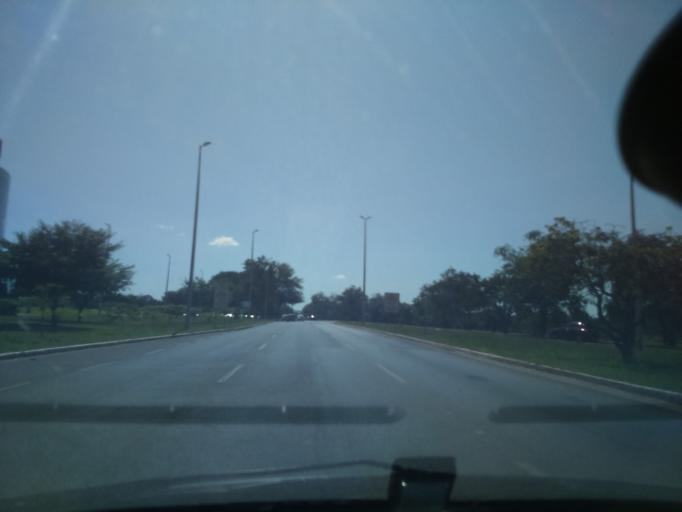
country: BR
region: Federal District
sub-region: Brasilia
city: Brasilia
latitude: -15.8090
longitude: -47.8596
